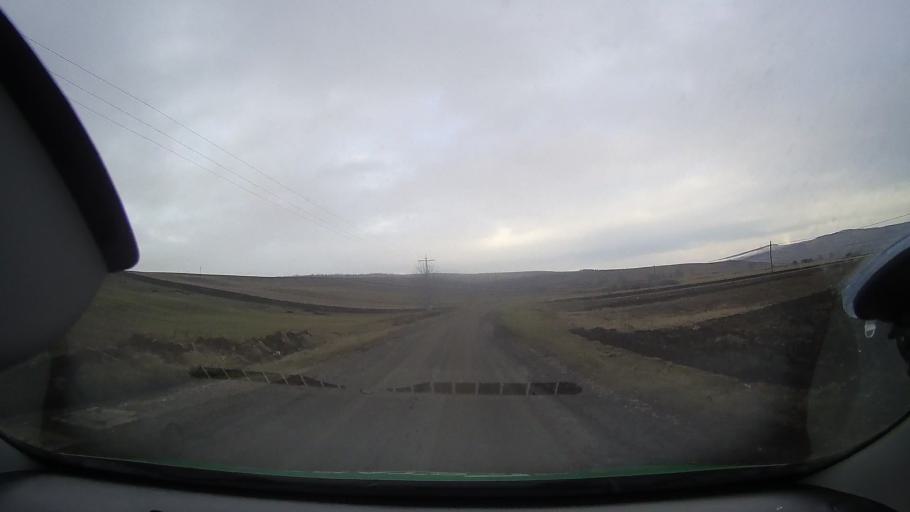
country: RO
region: Mures
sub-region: Comuna Bichis
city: Bichis
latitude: 46.3841
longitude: 24.0800
